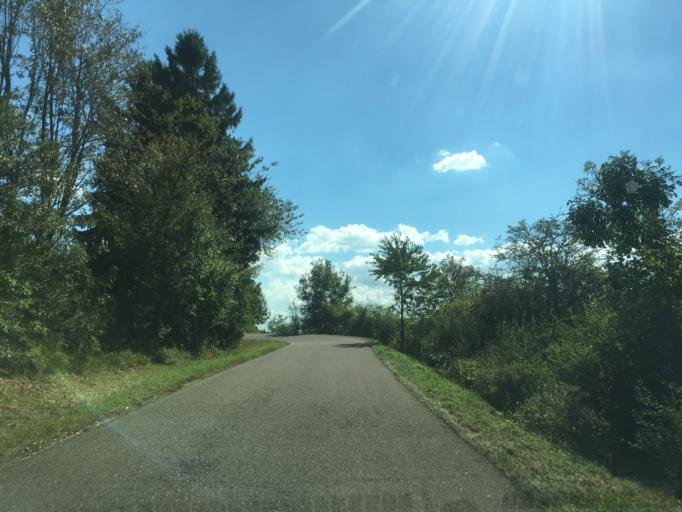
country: DE
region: Baden-Wuerttemberg
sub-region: Tuebingen Region
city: Pfullingen
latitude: 48.4113
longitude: 9.2144
